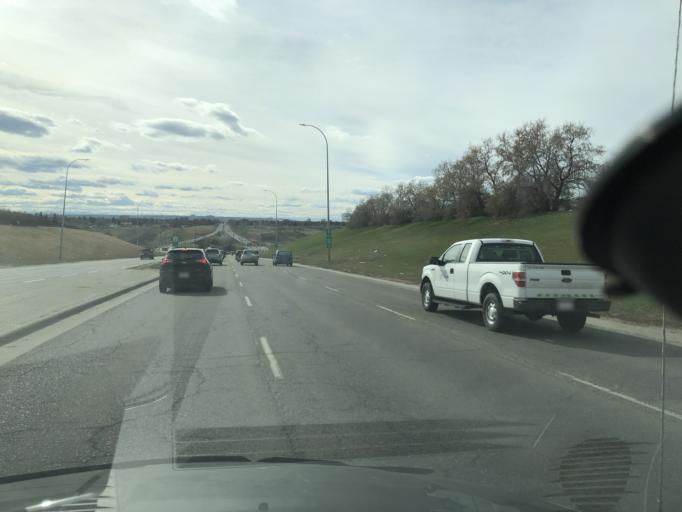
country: CA
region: Alberta
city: Calgary
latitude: 51.0670
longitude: -114.0161
